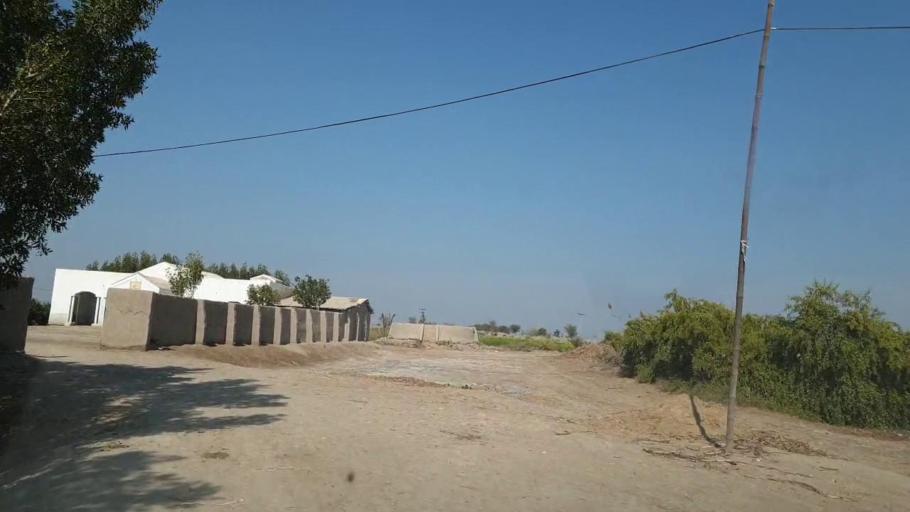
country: PK
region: Sindh
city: Mirpur Khas
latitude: 25.7415
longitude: 69.0919
